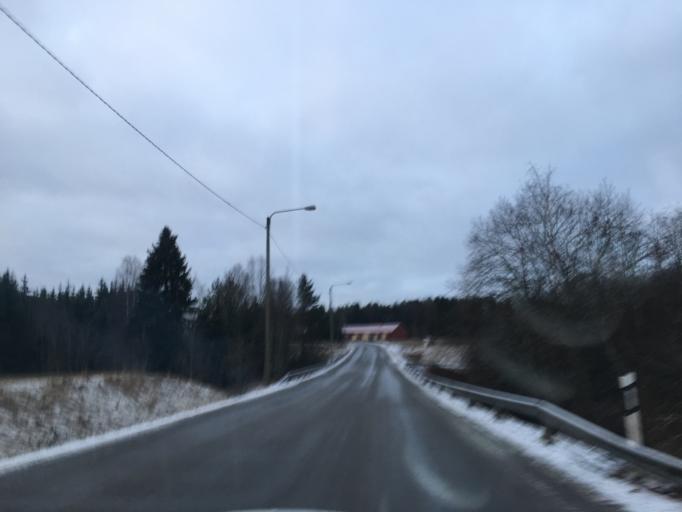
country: FI
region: Varsinais-Suomi
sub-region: Loimaa
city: Aura
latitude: 60.5985
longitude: 22.5379
